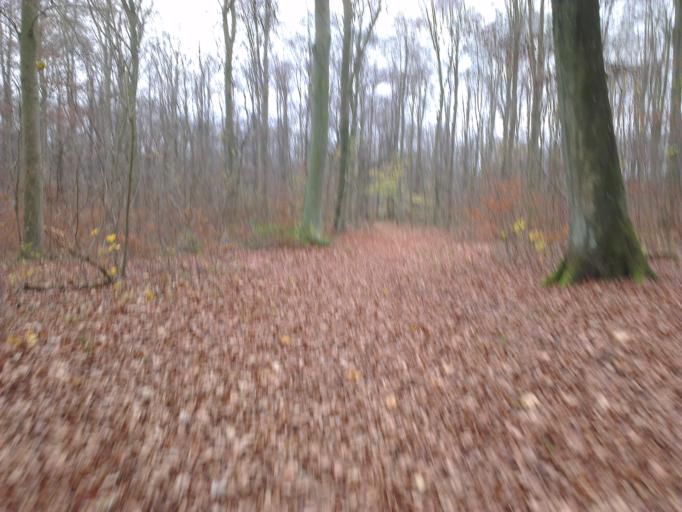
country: DK
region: Capital Region
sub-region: Frederikssund Kommune
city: Jaegerspris
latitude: 55.8624
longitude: 11.9838
